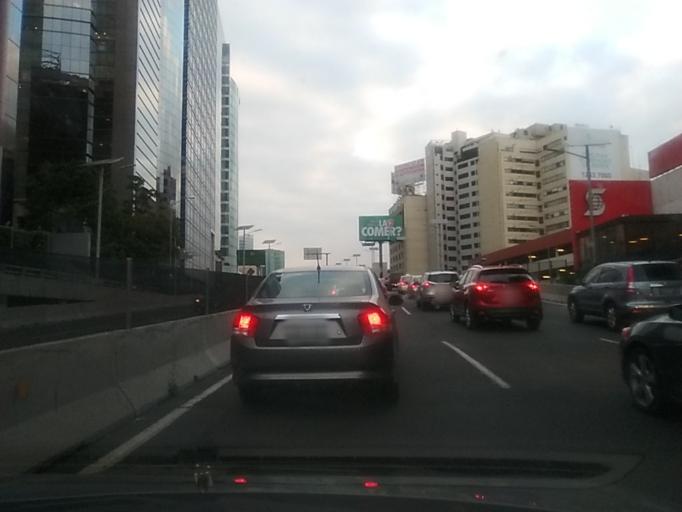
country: MX
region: Mexico City
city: Miguel Hidalgo
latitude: 19.4283
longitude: -99.2036
